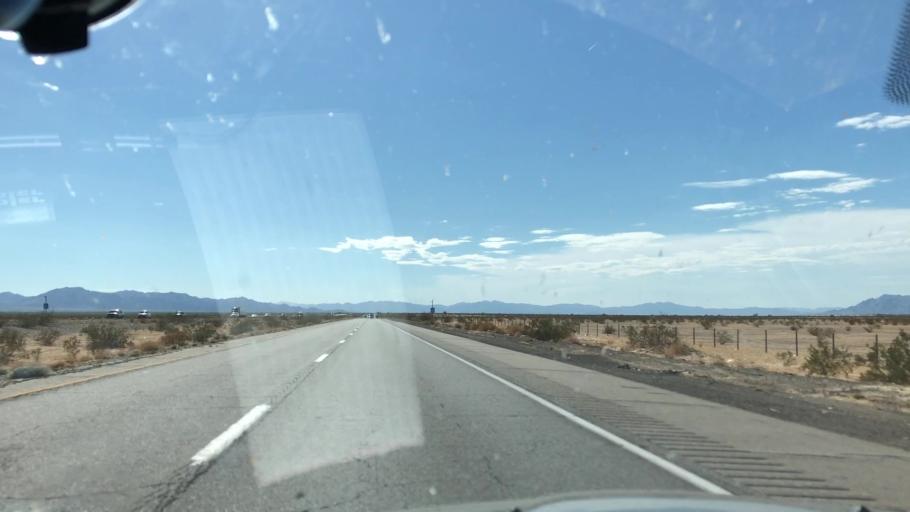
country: US
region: California
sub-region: Riverside County
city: Mesa Verde
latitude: 33.6411
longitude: -115.1011
